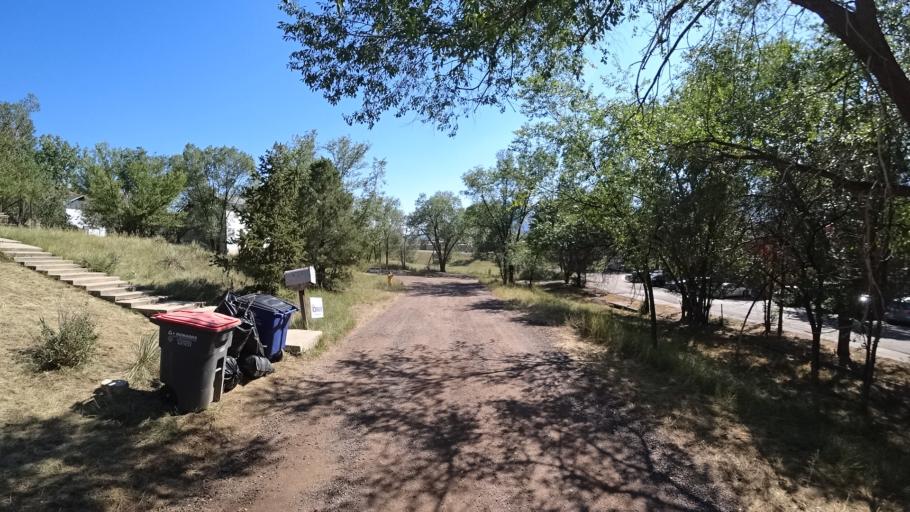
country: US
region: Colorado
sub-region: El Paso County
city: Colorado Springs
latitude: 38.8521
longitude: -104.8480
